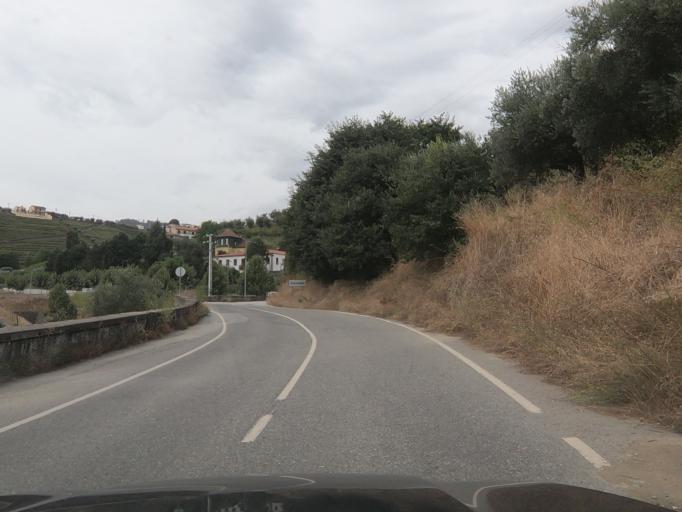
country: PT
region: Vila Real
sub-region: Santa Marta de Penaguiao
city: Santa Marta de Penaguiao
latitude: 41.2184
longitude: -7.7809
